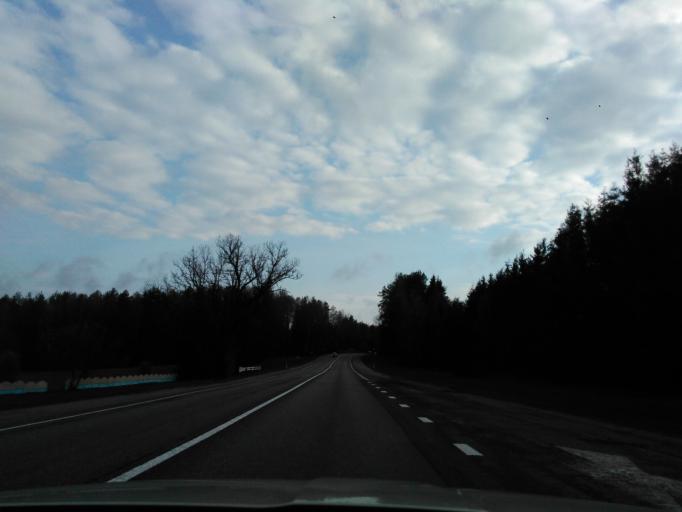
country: BY
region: Minsk
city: Lahoysk
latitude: 54.2894
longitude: 27.8713
